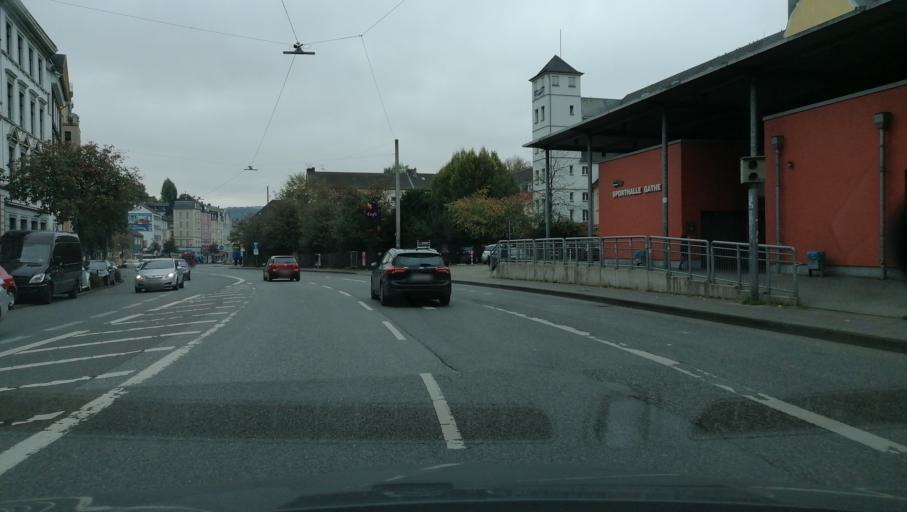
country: DE
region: North Rhine-Westphalia
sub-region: Regierungsbezirk Dusseldorf
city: Wuppertal
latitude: 51.2649
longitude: 7.1472
